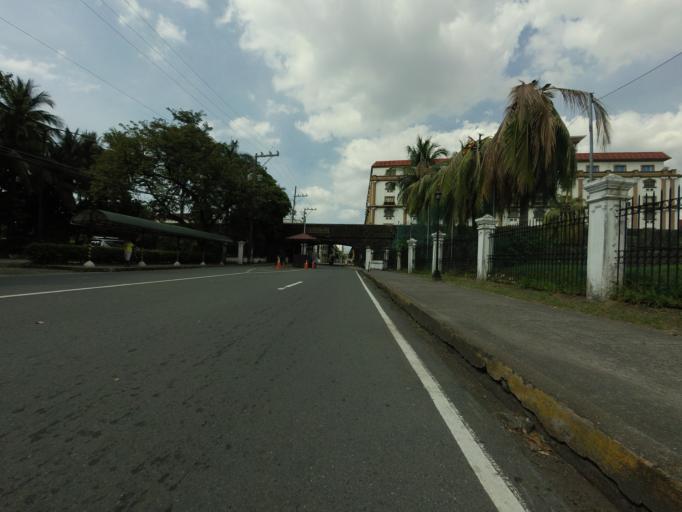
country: PH
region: Metro Manila
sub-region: City of Manila
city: Port Area
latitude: 14.5862
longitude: 120.9781
